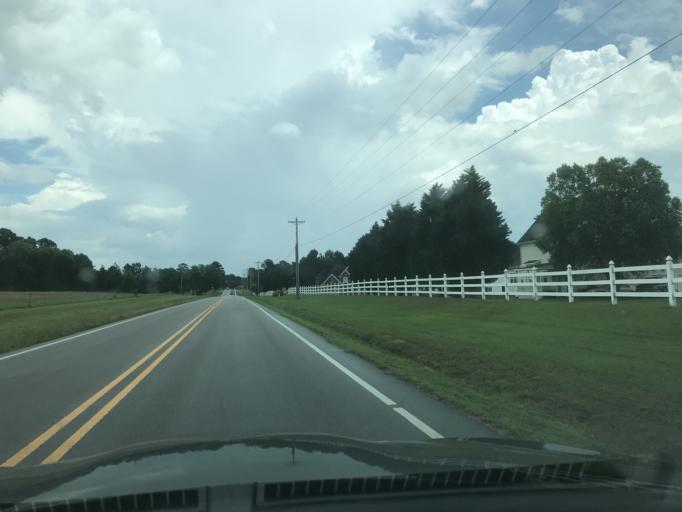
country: US
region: North Carolina
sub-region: Wake County
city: Knightdale
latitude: 35.8379
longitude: -78.4958
